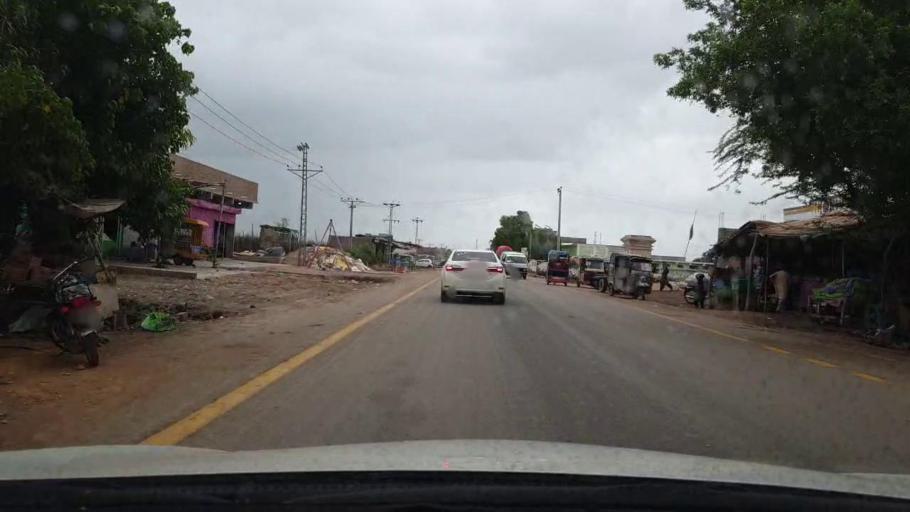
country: PK
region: Sindh
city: Badin
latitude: 24.6554
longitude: 68.8190
